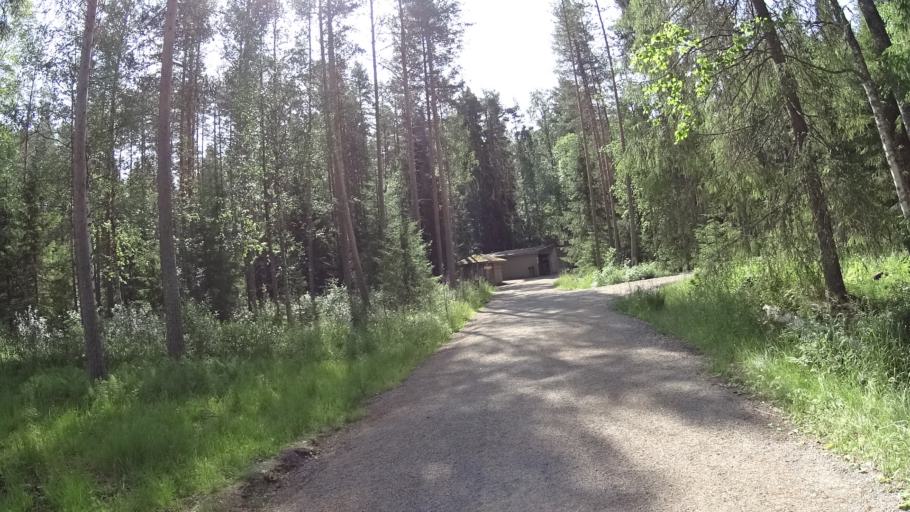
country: FI
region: Southern Ostrobothnia
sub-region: Kuusiokunnat
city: AEhtaeri
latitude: 62.5396
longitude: 24.1842
